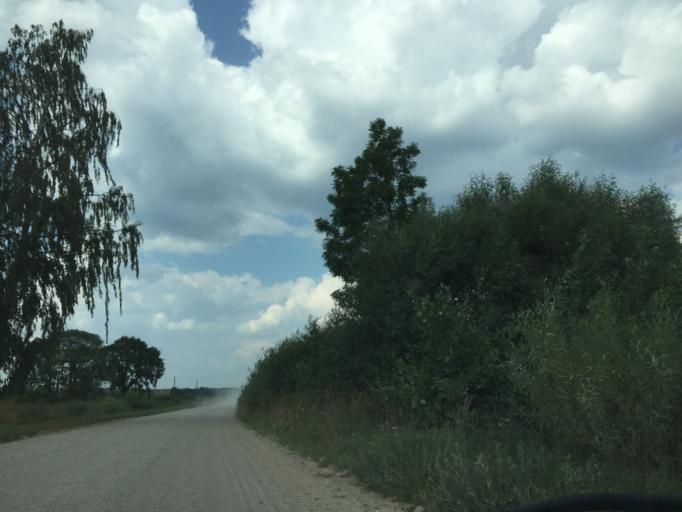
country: LT
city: Naujoji Akmene
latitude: 56.3781
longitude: 23.0485
